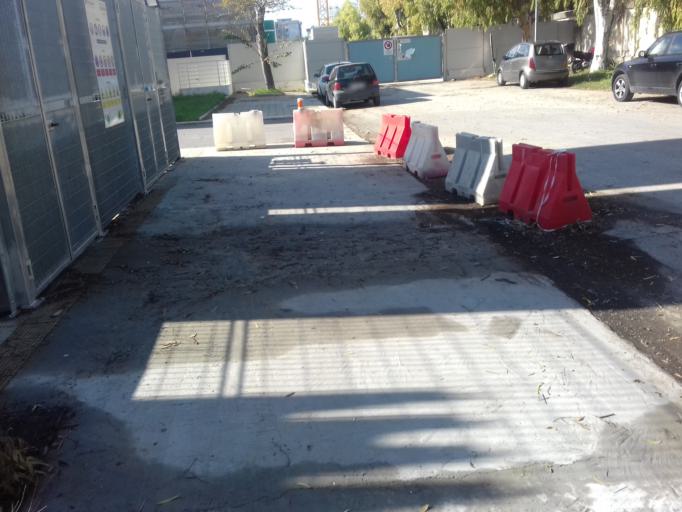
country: IT
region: Apulia
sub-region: Provincia di Bari
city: Bari
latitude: 41.1145
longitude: 16.8595
